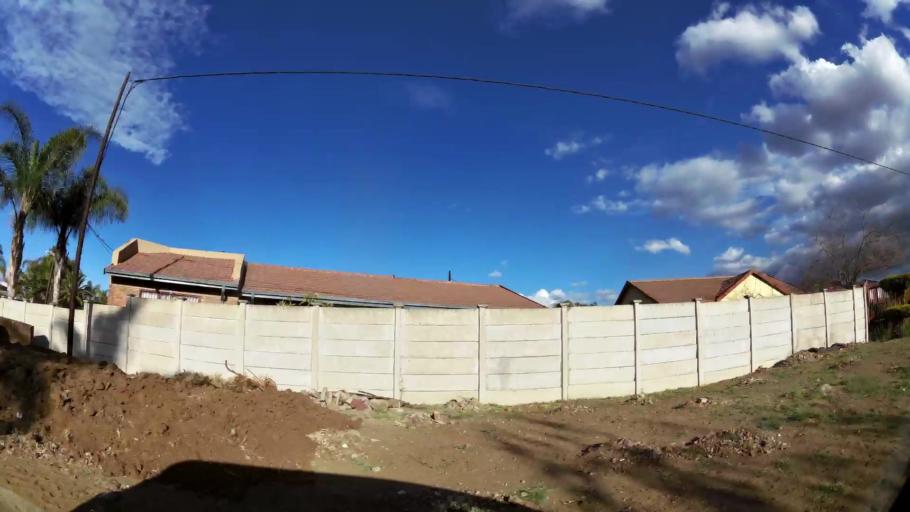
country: ZA
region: Limpopo
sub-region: Capricorn District Municipality
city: Polokwane
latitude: -23.9170
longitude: 29.4299
